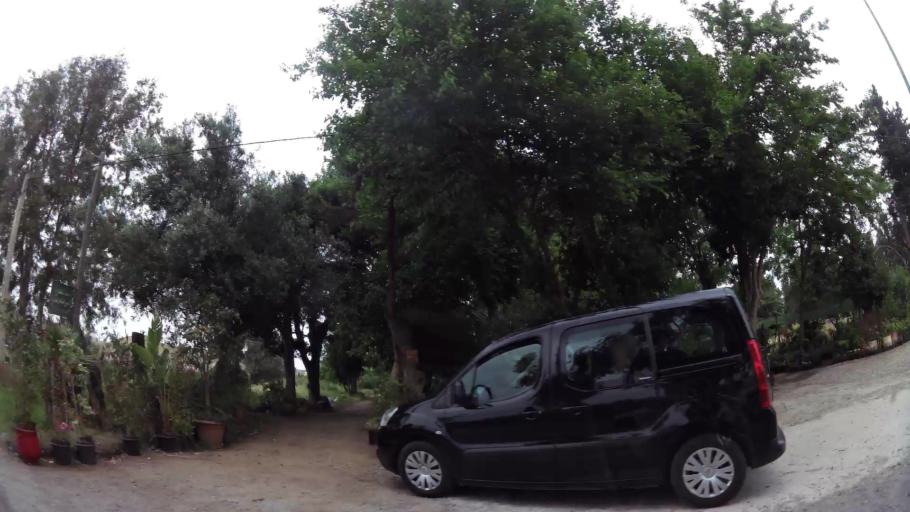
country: MA
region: Rabat-Sale-Zemmour-Zaer
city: Sale
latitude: 33.9991
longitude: -6.7732
